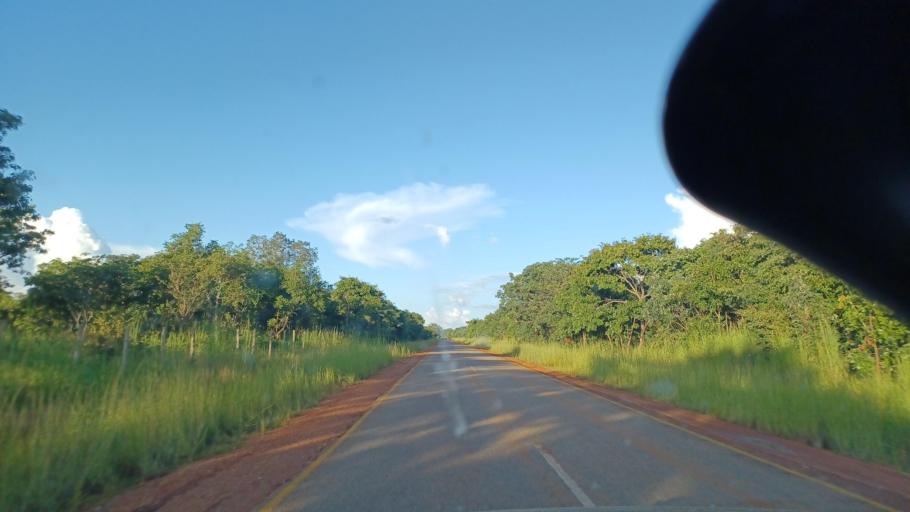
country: ZM
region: North-Western
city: Kalengwa
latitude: -13.1438
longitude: 25.0576
